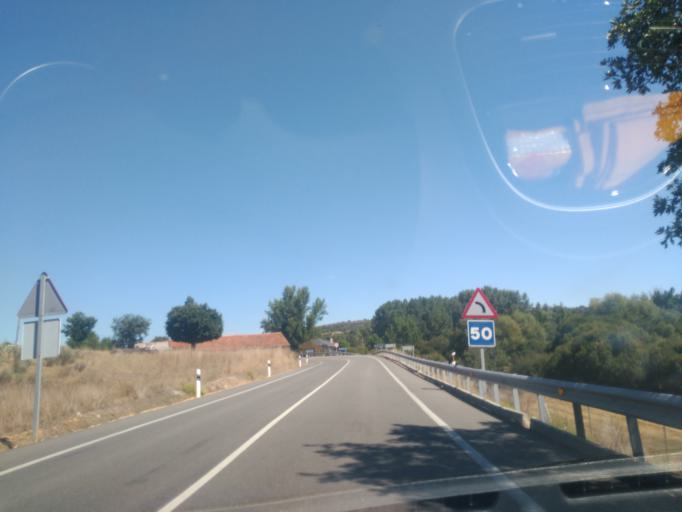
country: ES
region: Castille and Leon
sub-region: Provincia de Zamora
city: Ferreras de Arriba
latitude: 41.9627
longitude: -6.2183
